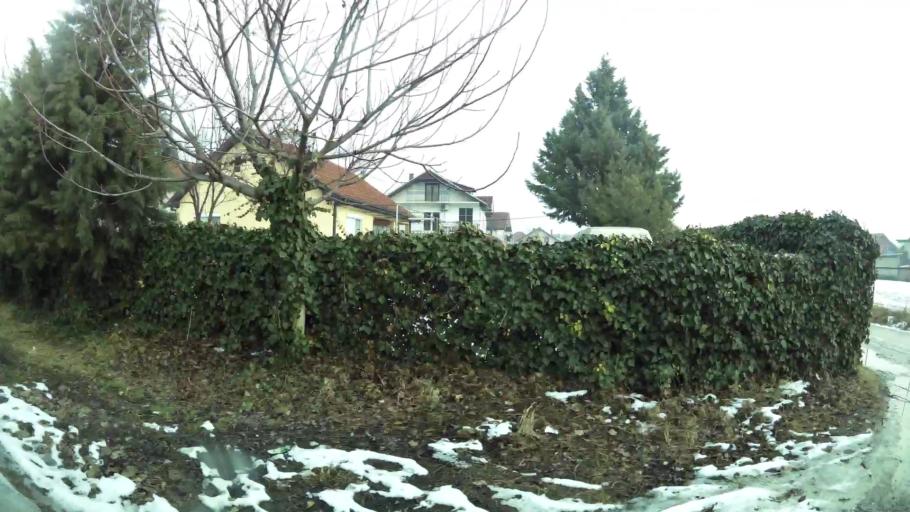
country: MK
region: Ilinden
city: Ilinden
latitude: 41.9928
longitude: 21.5826
